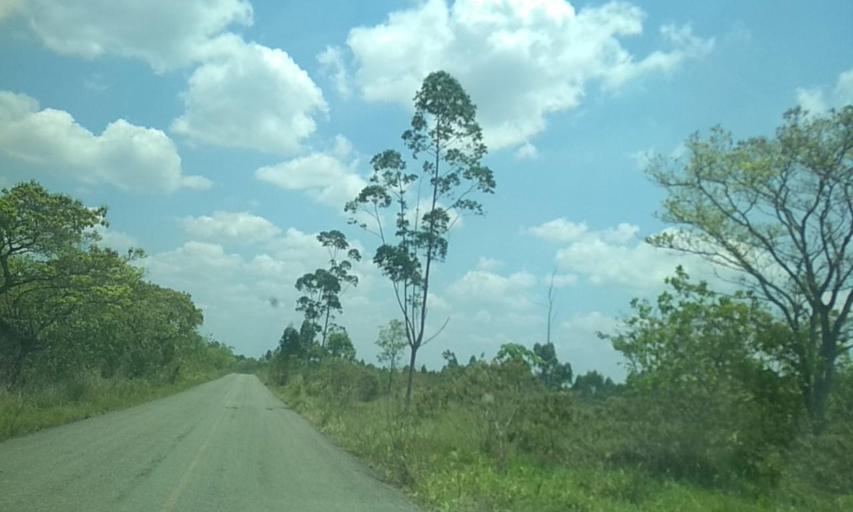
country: MX
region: Tabasco
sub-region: Huimanguillo
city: Francisco Rueda
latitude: 17.7820
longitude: -93.8280
